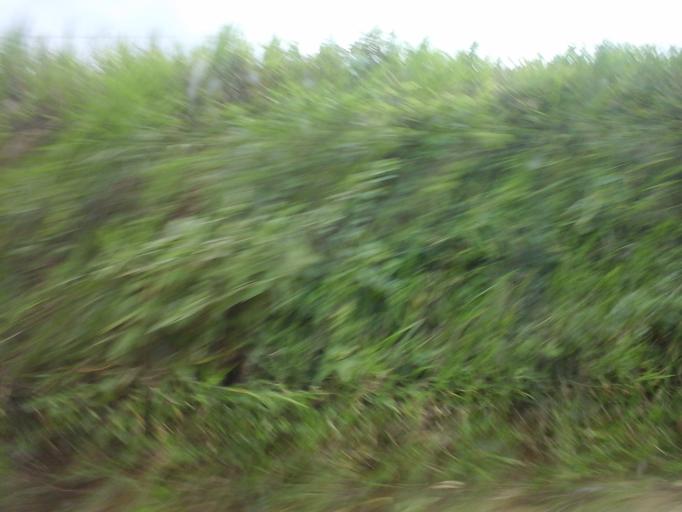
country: CO
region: Caqueta
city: El Doncello
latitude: 1.6411
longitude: -75.1543
